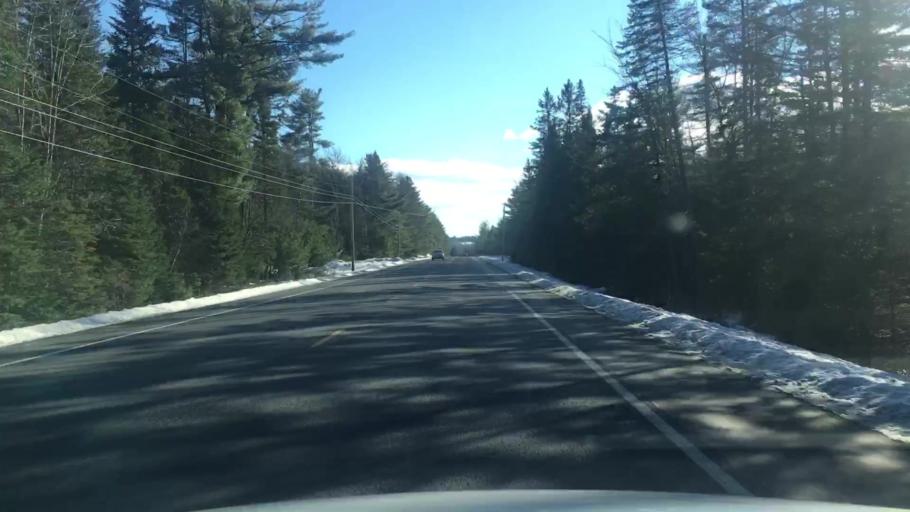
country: US
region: Maine
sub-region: Somerset County
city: Madison
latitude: 44.9175
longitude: -69.8240
